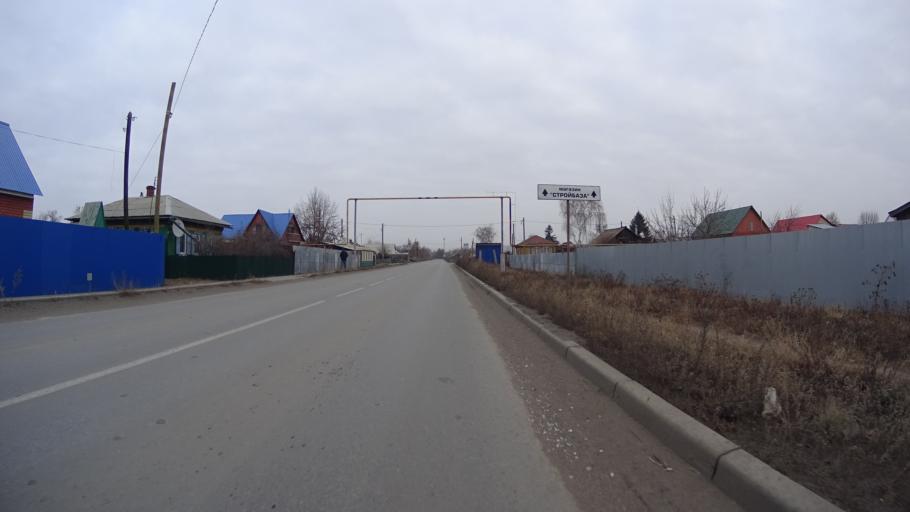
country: RU
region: Chelyabinsk
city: Troitsk
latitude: 54.1064
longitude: 61.5677
